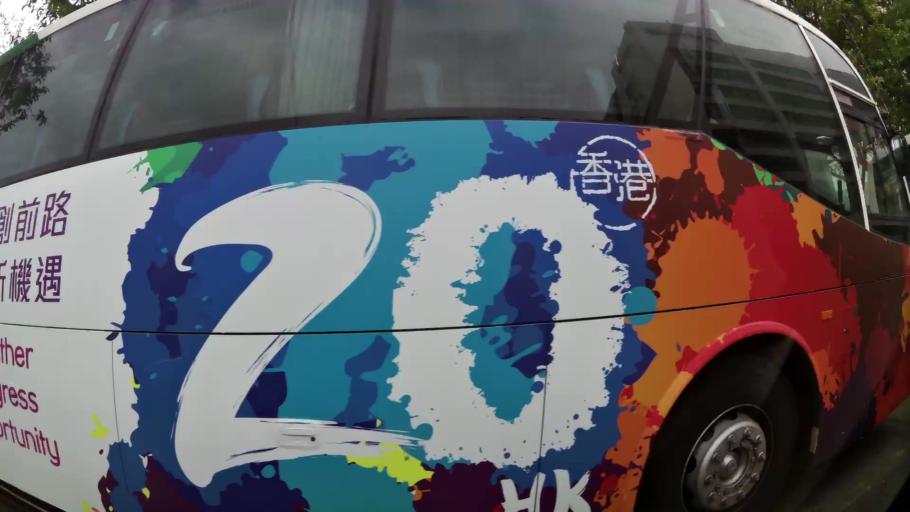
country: HK
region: Wanchai
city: Wan Chai
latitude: 22.2735
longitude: 114.2428
